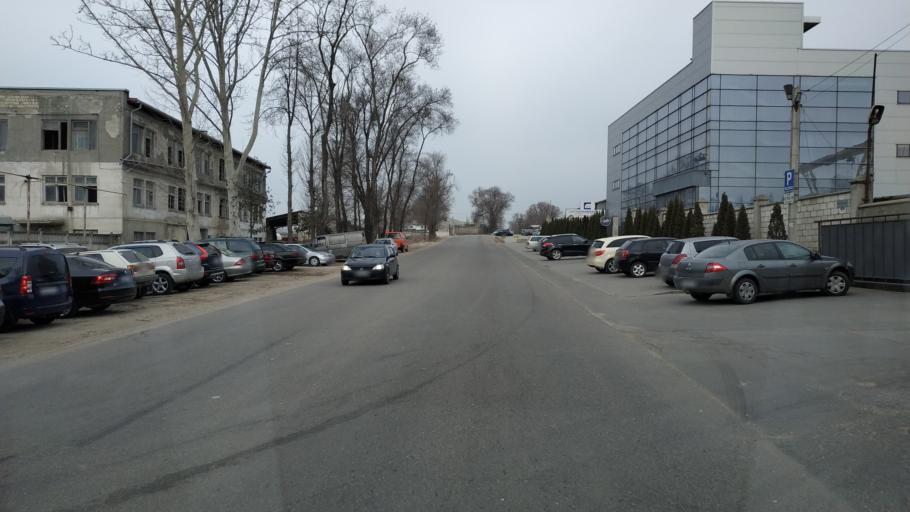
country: MD
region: Chisinau
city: Vatra
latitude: 47.0580
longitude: 28.7825
